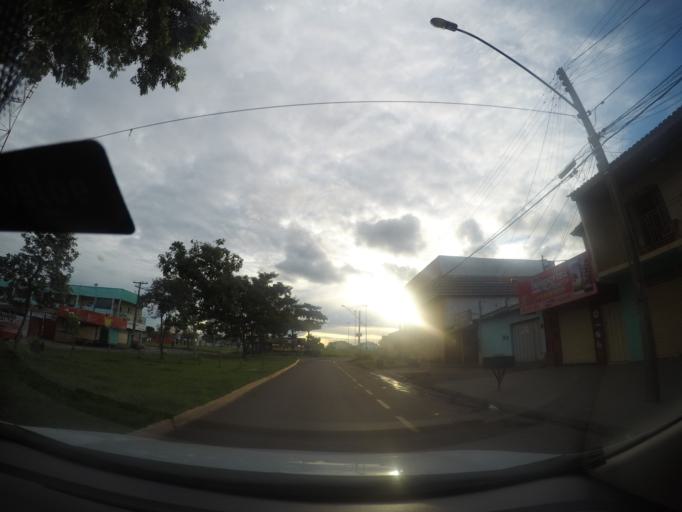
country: BR
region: Goias
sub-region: Goianira
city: Goianira
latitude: -16.5888
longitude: -49.3751
